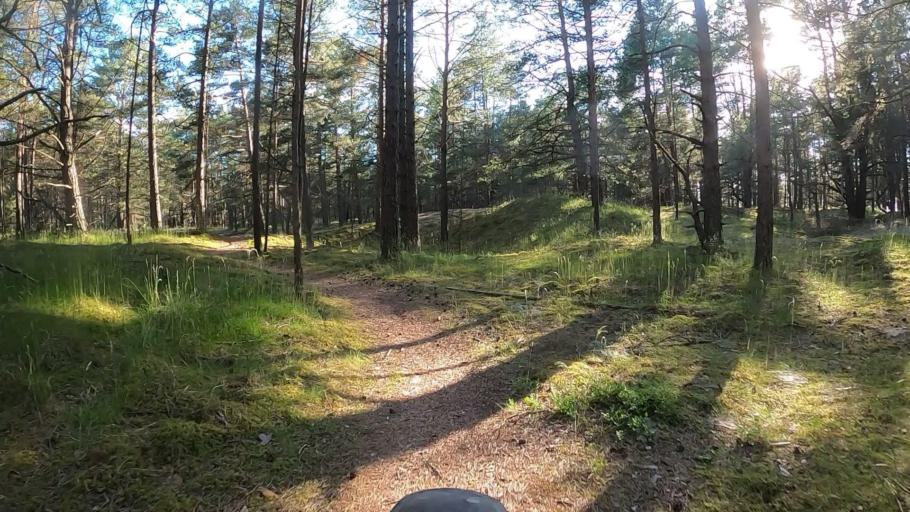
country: LV
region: Carnikava
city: Carnikava
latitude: 57.1331
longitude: 24.2302
